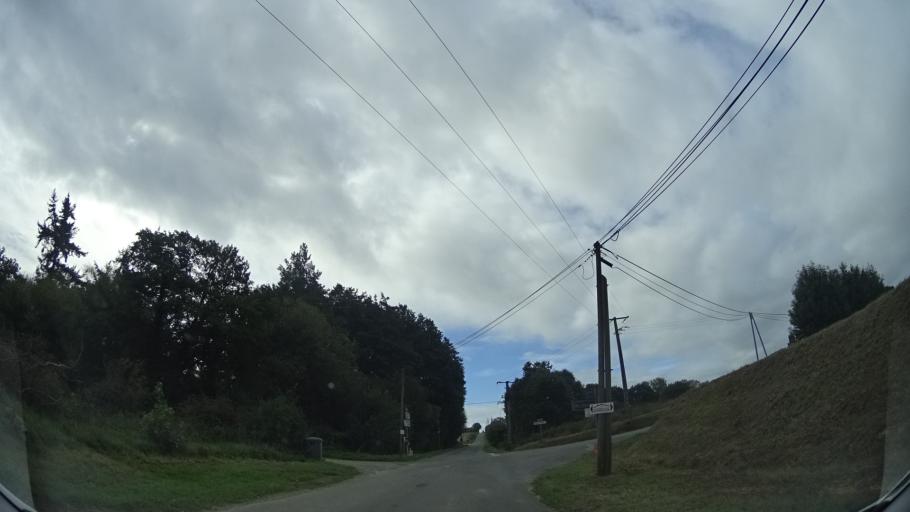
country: FR
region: Brittany
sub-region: Departement d'Ille-et-Vilaine
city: Tinteniac
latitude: 48.2869
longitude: -1.8517
